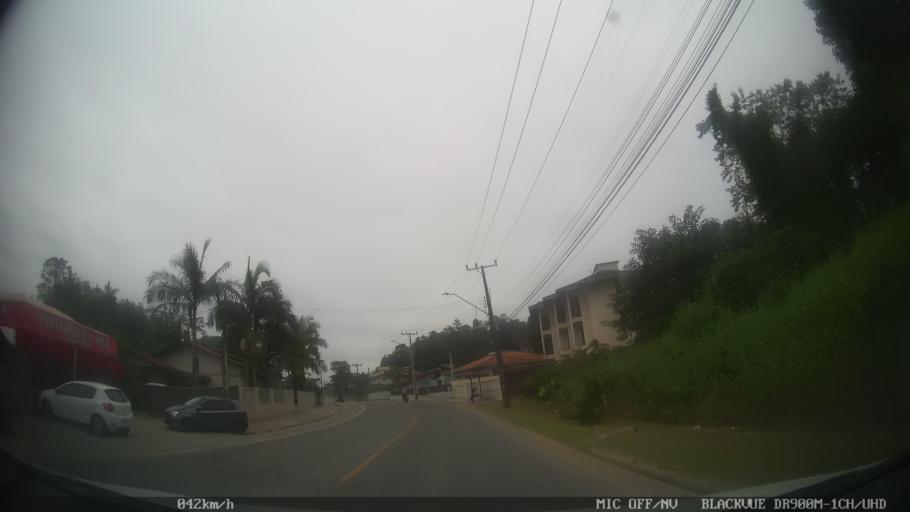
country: BR
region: Santa Catarina
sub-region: Joinville
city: Joinville
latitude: -26.3462
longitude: -48.8176
